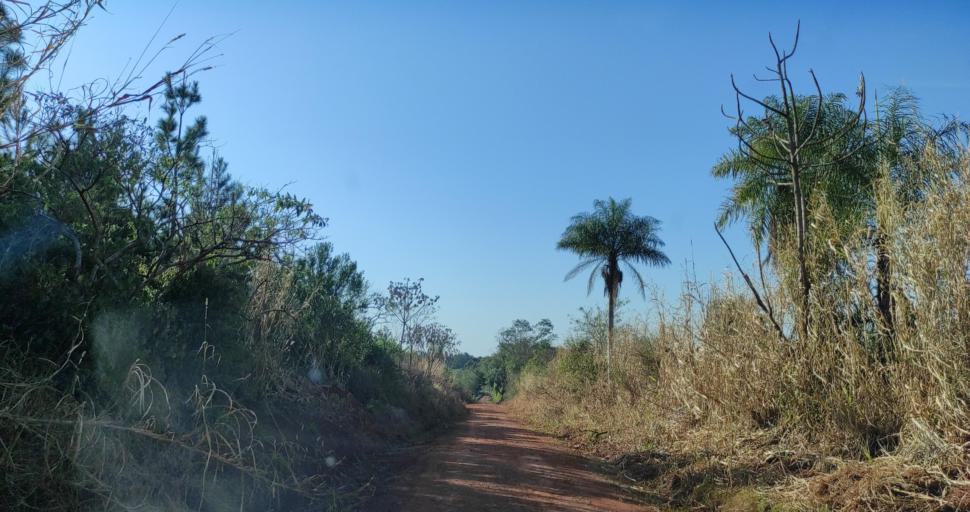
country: AR
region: Misiones
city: Capiovi
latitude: -26.8816
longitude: -55.1077
